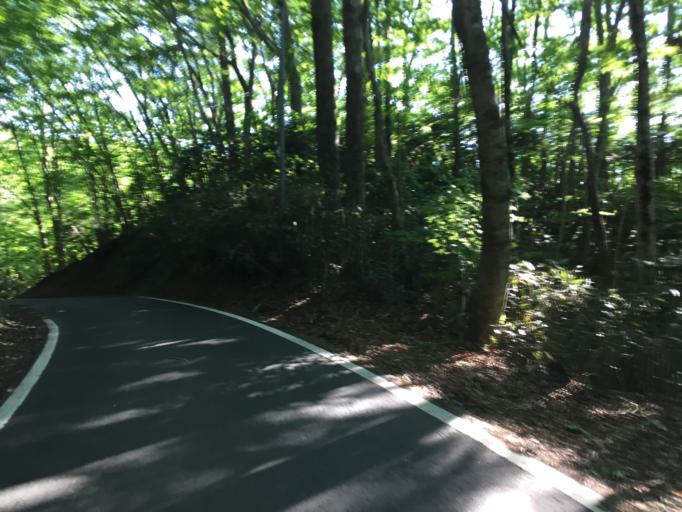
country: JP
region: Ibaraki
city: Kitaibaraki
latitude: 36.8972
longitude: 140.6145
